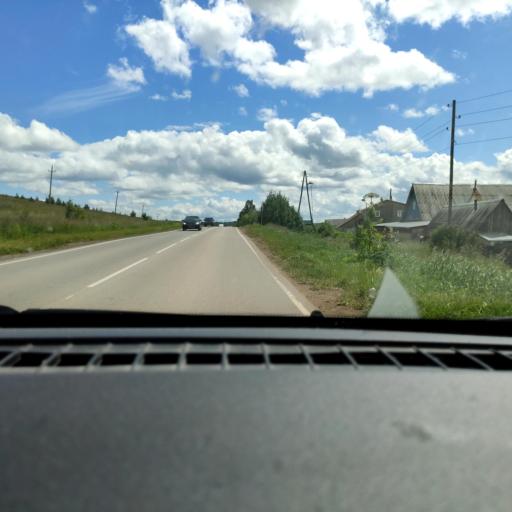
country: RU
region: Perm
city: Overyata
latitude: 58.1222
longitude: 55.8141
